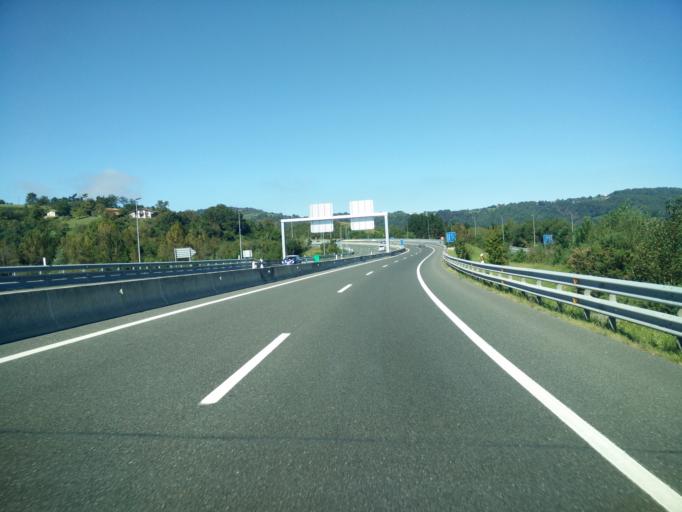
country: ES
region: Basque Country
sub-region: Provincia de Guipuzcoa
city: Usurbil
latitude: 43.2893
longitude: -2.0367
